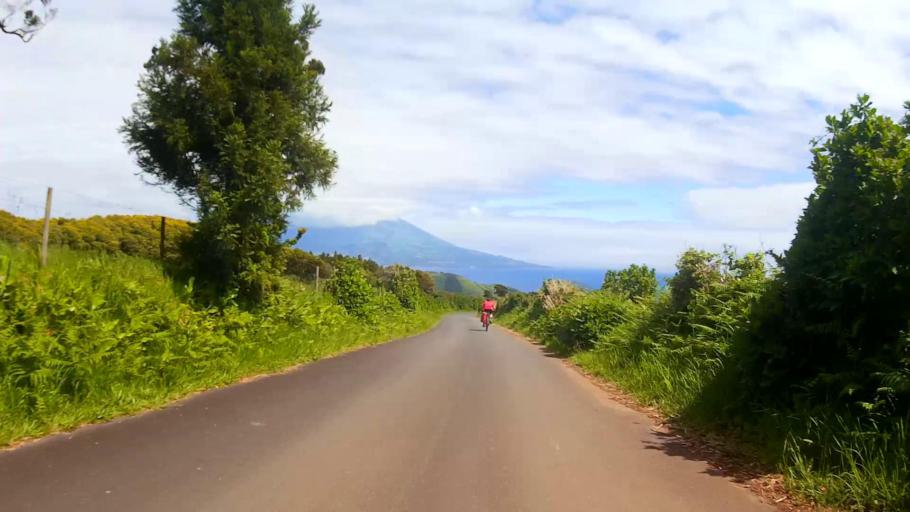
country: PT
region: Azores
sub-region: Horta
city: Horta
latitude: 38.5524
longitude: -28.6732
